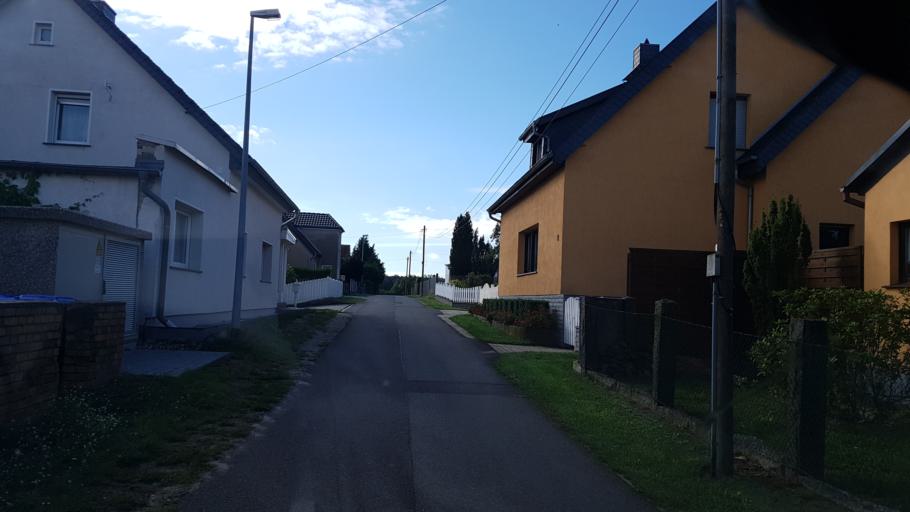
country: DE
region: Brandenburg
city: Tschernitz
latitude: 51.6377
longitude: 14.5952
